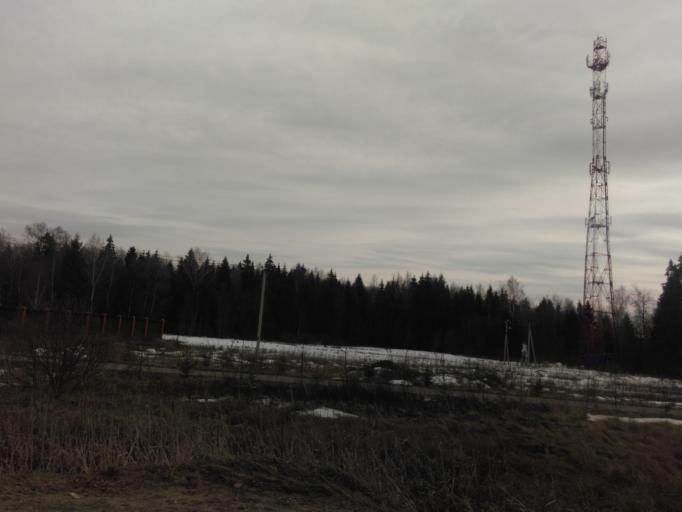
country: RU
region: Moskovskaya
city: Kolyubakino
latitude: 55.7007
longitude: 36.5976
